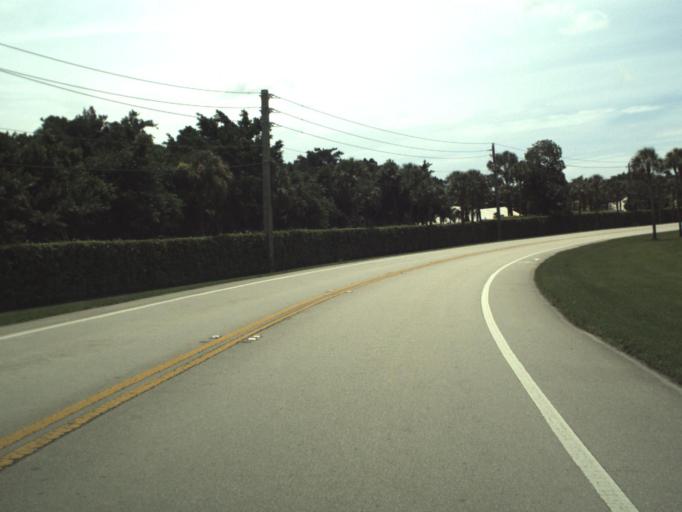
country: US
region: Florida
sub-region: Palm Beach County
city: Juno Beach
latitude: 26.8434
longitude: -80.0517
